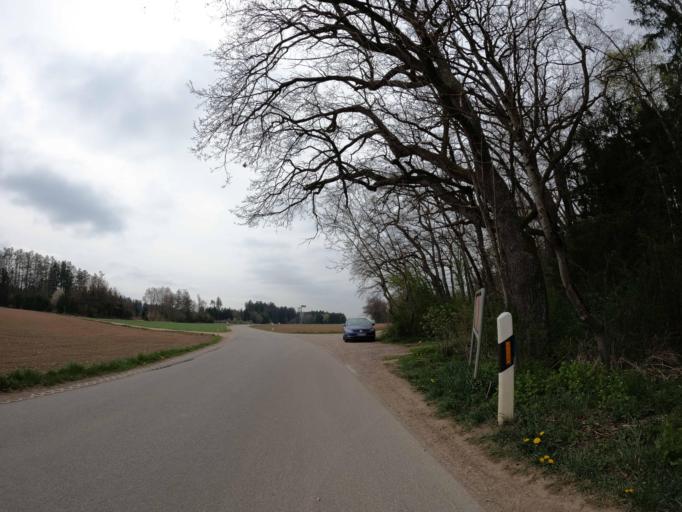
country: DE
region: Bavaria
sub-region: Upper Bavaria
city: Anzing
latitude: 48.1260
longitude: 11.8244
